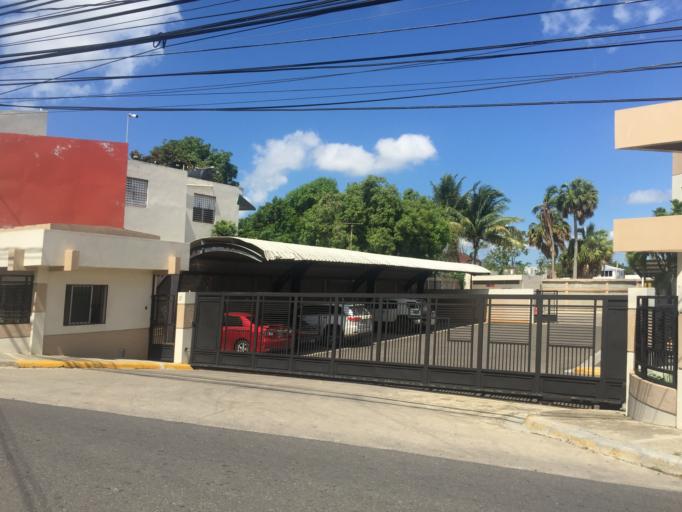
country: DO
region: Santiago
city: Santiago de los Caballeros
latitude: 19.4645
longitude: -70.6608
